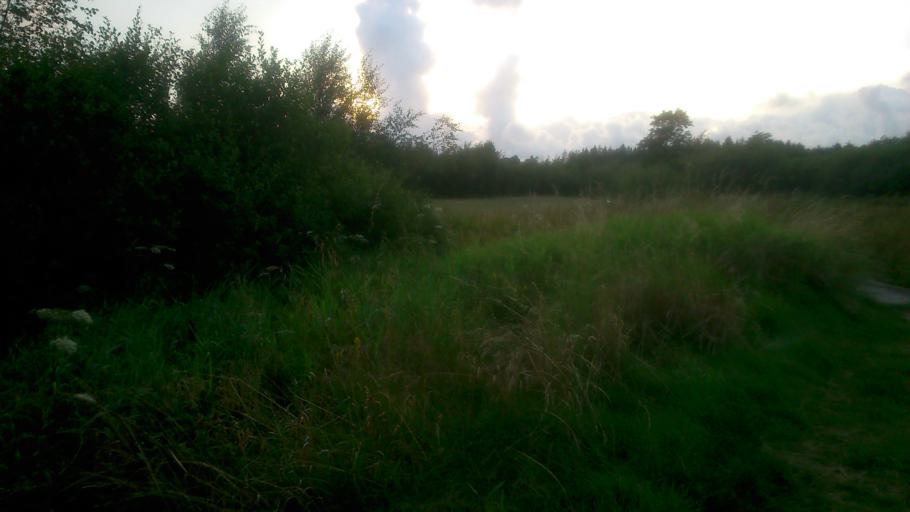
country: DK
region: Central Jutland
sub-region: Ringkobing-Skjern Kommune
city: Skjern
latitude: 56.0075
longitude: 8.4762
